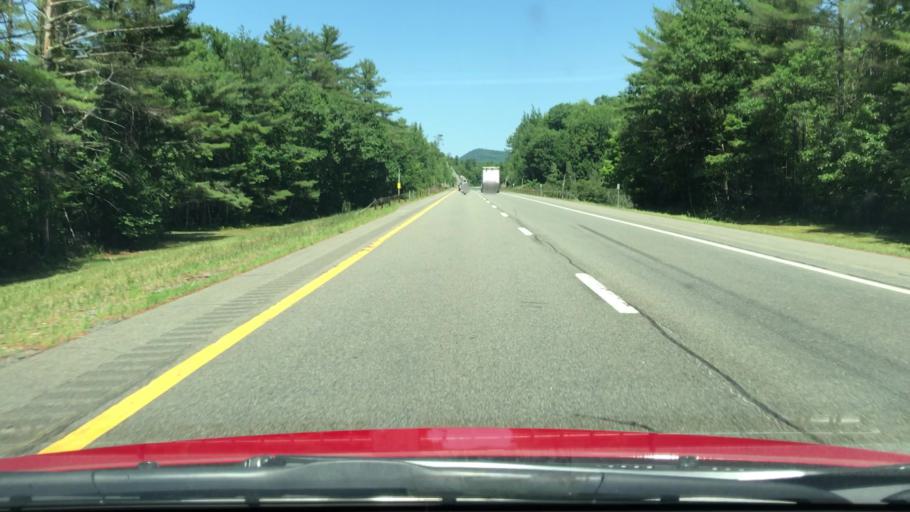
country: US
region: New York
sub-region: Essex County
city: Elizabethtown
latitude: 44.3306
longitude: -73.5315
